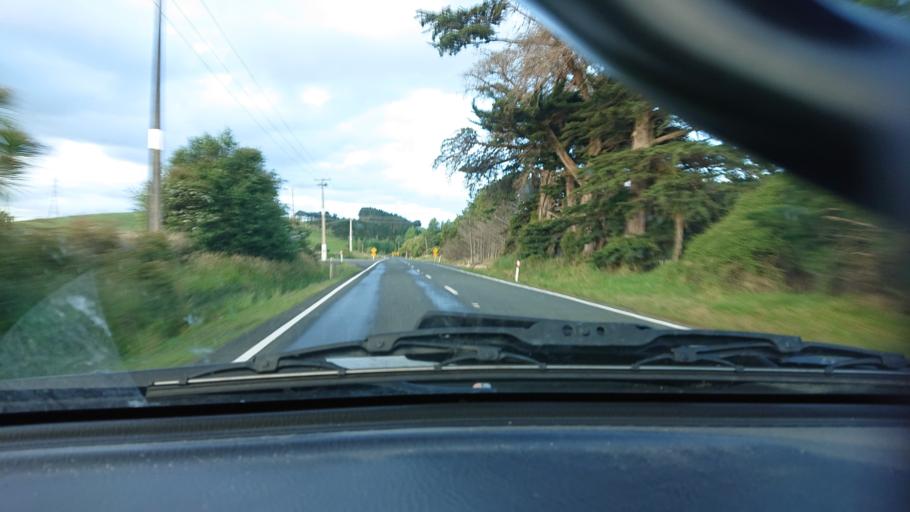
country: NZ
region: Auckland
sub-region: Auckland
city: Parakai
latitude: -36.4853
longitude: 174.4497
